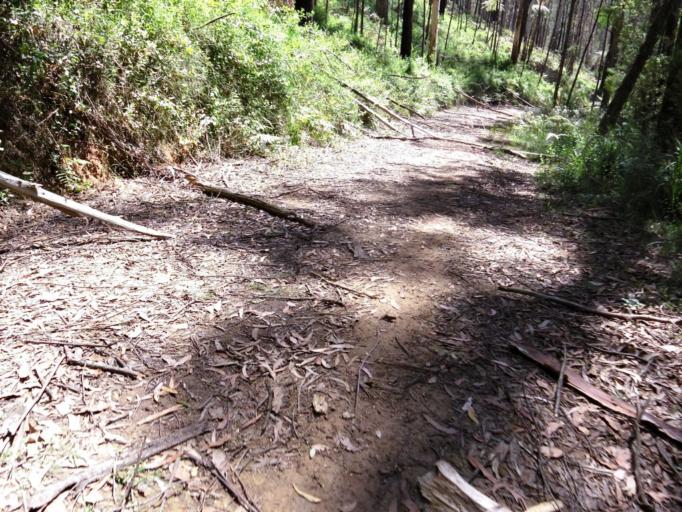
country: AU
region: Victoria
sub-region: Yarra Ranges
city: Millgrove
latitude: -37.8541
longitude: 145.7573
